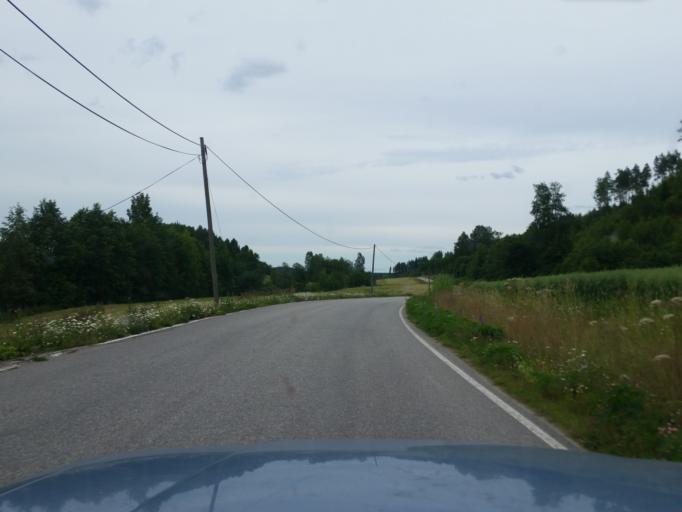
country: FI
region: Uusimaa
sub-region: Helsinki
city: Sammatti
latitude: 60.4399
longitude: 23.8414
